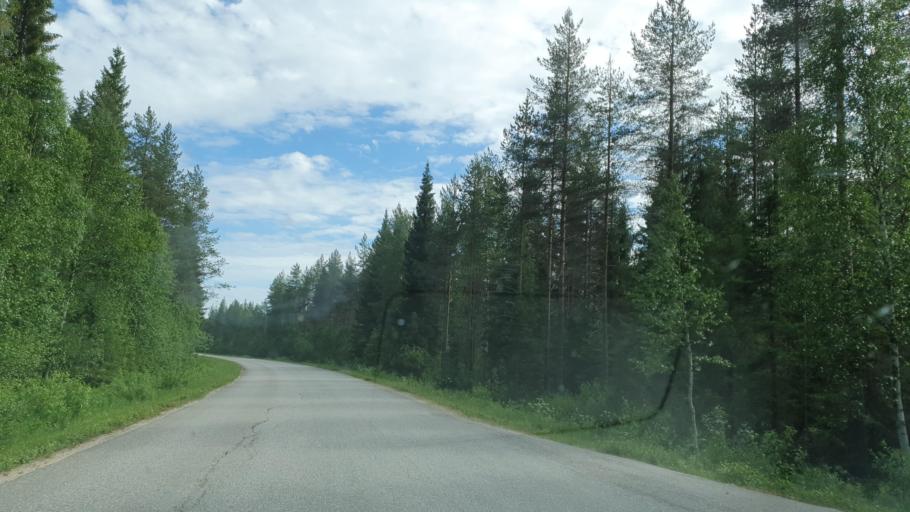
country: FI
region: Kainuu
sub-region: Kehys-Kainuu
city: Suomussalmi
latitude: 64.5710
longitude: 29.1288
